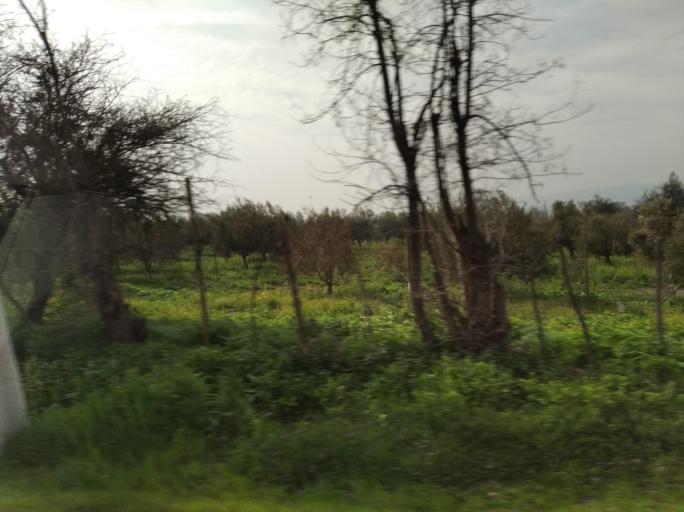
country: CL
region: Santiago Metropolitan
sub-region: Provincia de Chacabuco
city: Lampa
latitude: -33.1672
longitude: -70.8942
